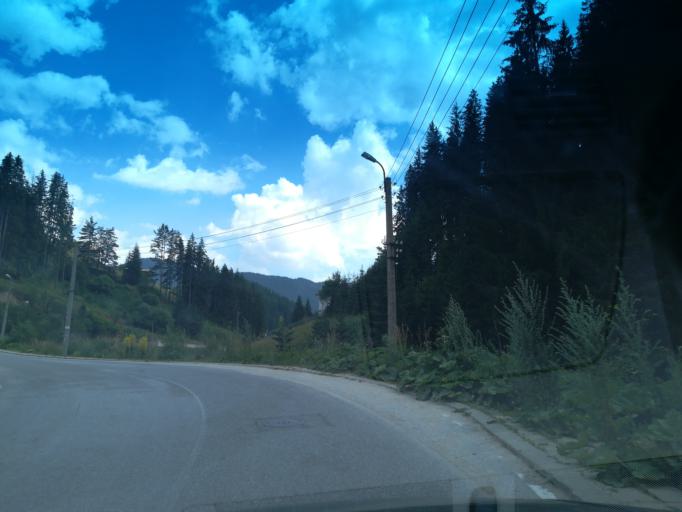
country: BG
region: Smolyan
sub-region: Obshtina Smolyan
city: Smolyan
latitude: 41.6556
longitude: 24.6345
